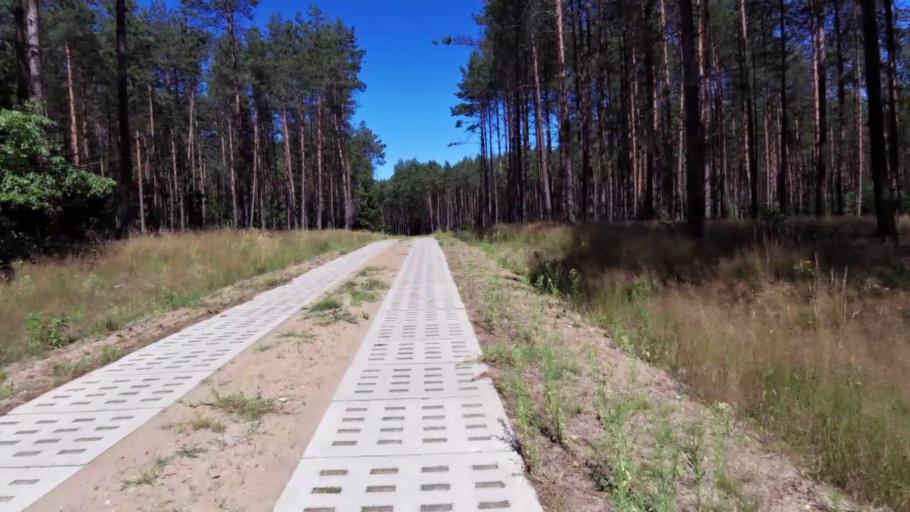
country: PL
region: West Pomeranian Voivodeship
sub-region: Powiat szczecinecki
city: Szczecinek
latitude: 53.6119
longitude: 16.6648
